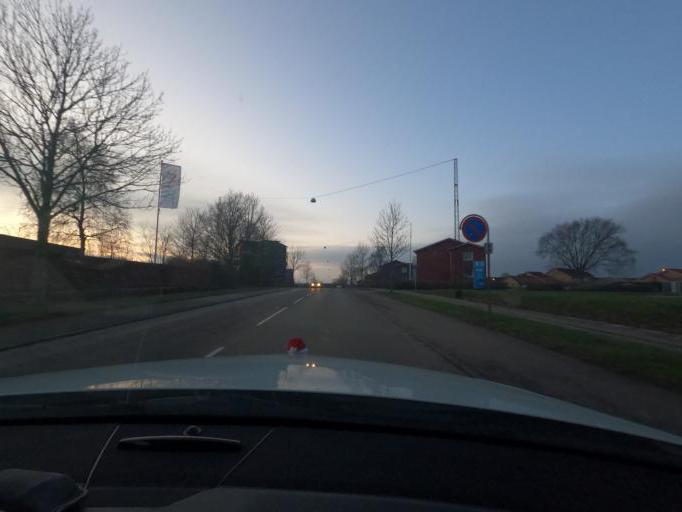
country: DK
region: South Denmark
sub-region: Sonderborg Kommune
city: Sonderborg
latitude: 54.9193
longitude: 9.7891
